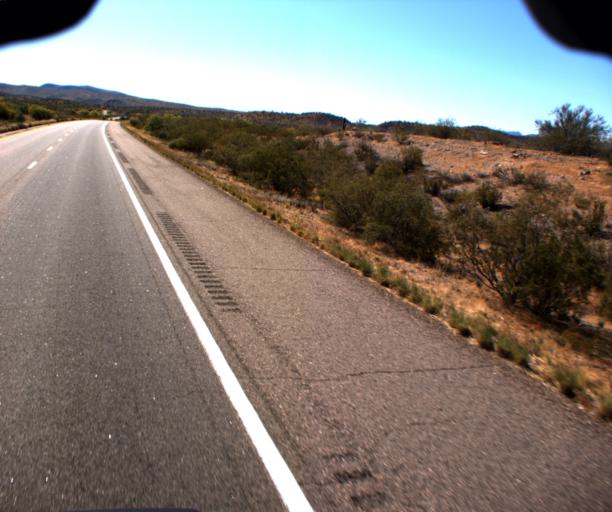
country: US
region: Arizona
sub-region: Yavapai County
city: Bagdad
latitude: 34.6292
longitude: -113.5420
